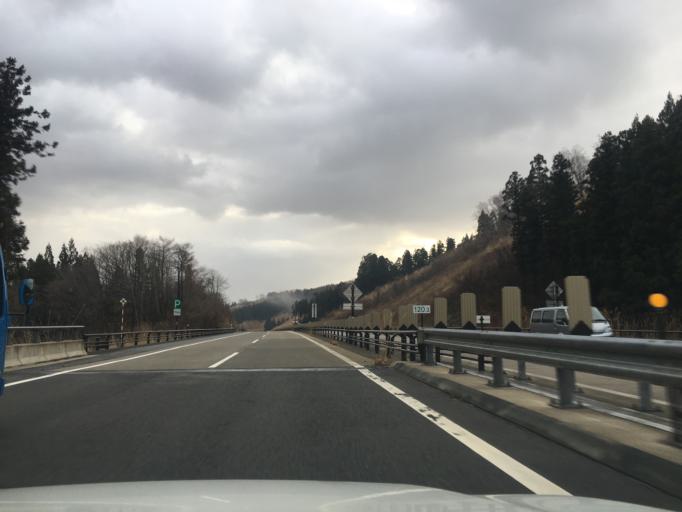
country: JP
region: Yamagata
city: Tsuruoka
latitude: 38.6970
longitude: 139.7073
